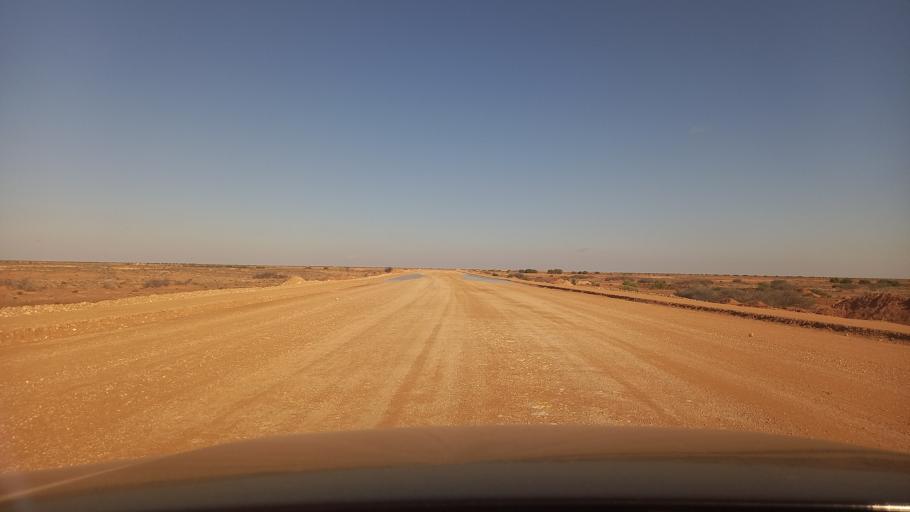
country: TN
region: Tataouine
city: Tataouine
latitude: 33.1369
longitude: 10.5050
